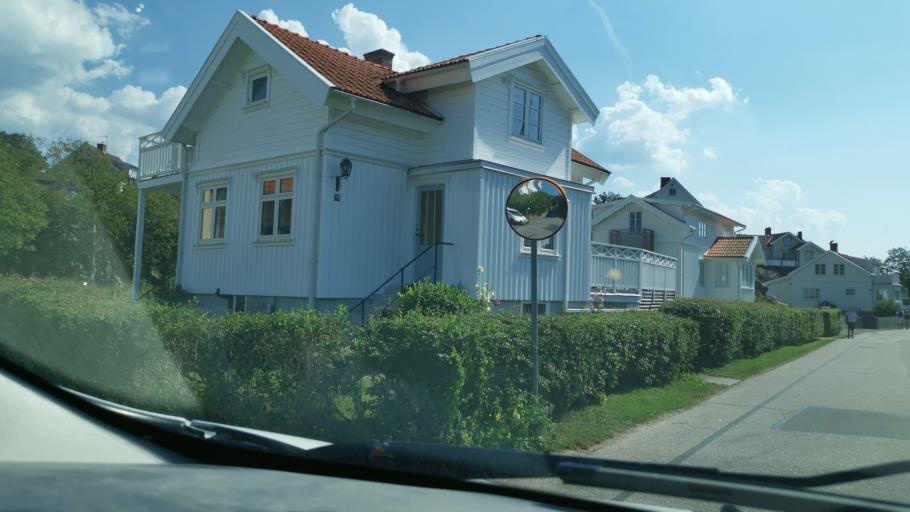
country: SE
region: Vaestra Goetaland
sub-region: Lysekils Kommun
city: Lysekil
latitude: 58.2144
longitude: 11.4199
